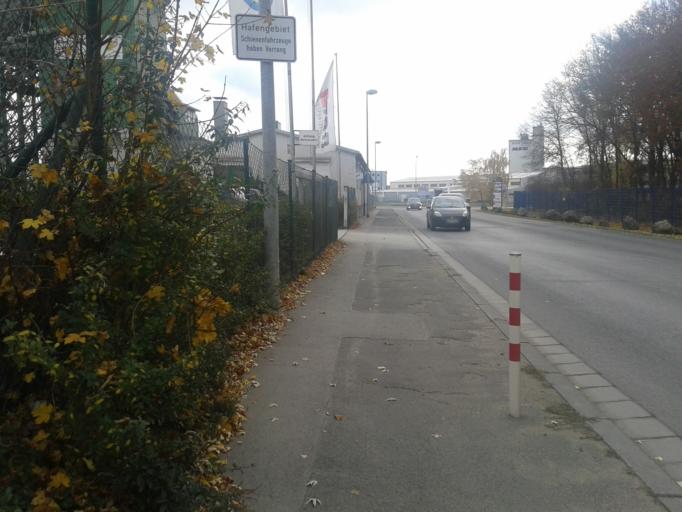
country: DE
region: Bavaria
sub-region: Upper Franconia
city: Hallstadt
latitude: 49.9141
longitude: 10.8620
